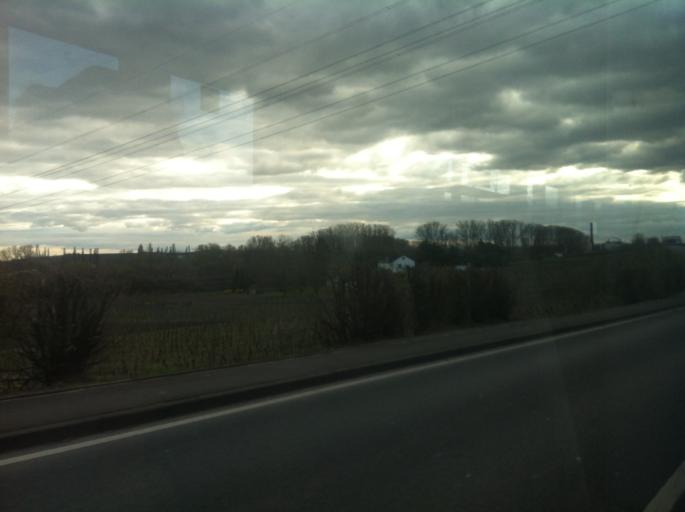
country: DE
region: Hesse
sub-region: Regierungsbezirk Darmstadt
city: Hochheim am Main
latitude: 50.0086
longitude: 8.3316
